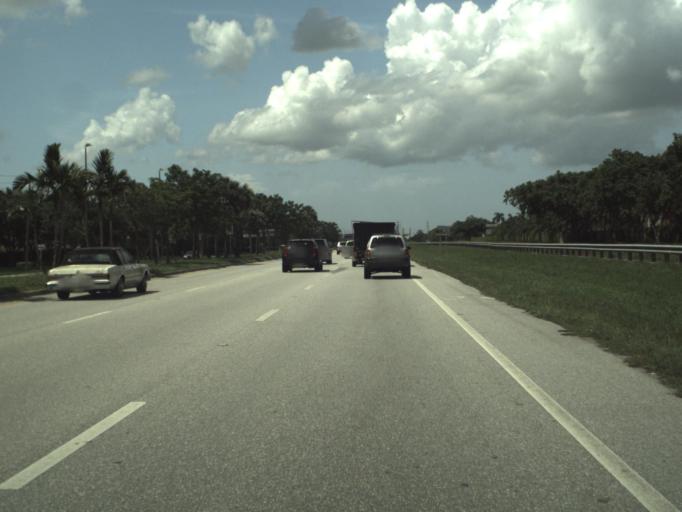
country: US
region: Florida
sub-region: Palm Beach County
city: Boca Pointe
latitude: 26.3395
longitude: -80.2030
